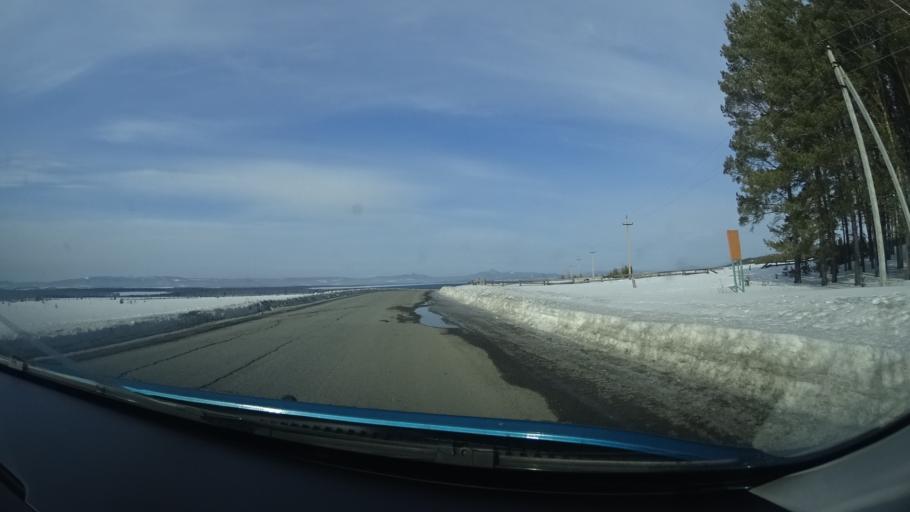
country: RU
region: Bashkortostan
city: Lomovka
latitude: 53.8292
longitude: 58.2812
